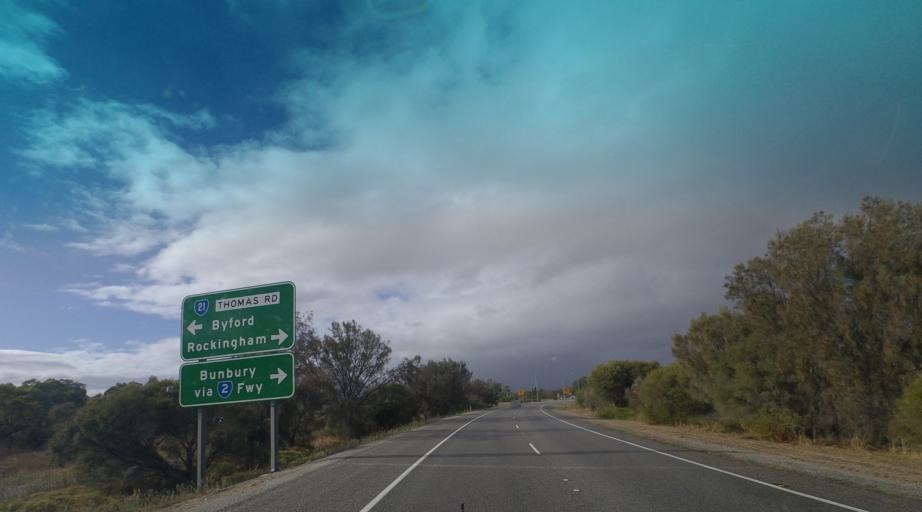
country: AU
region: Western Australia
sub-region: Serpentine-Jarrahdale
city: Oakford
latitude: -32.2047
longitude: 115.9690
